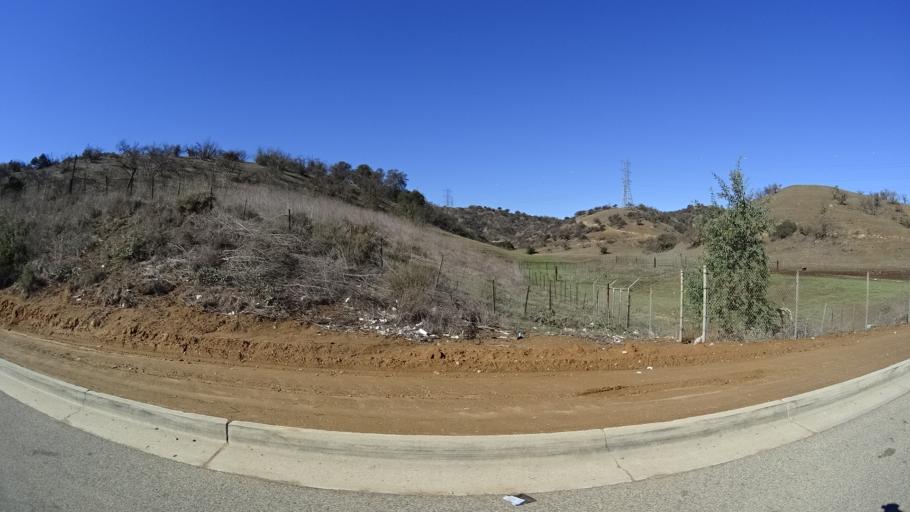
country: US
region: California
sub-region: Los Angeles County
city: Rowland Heights
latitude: 33.9564
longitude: -117.8625
